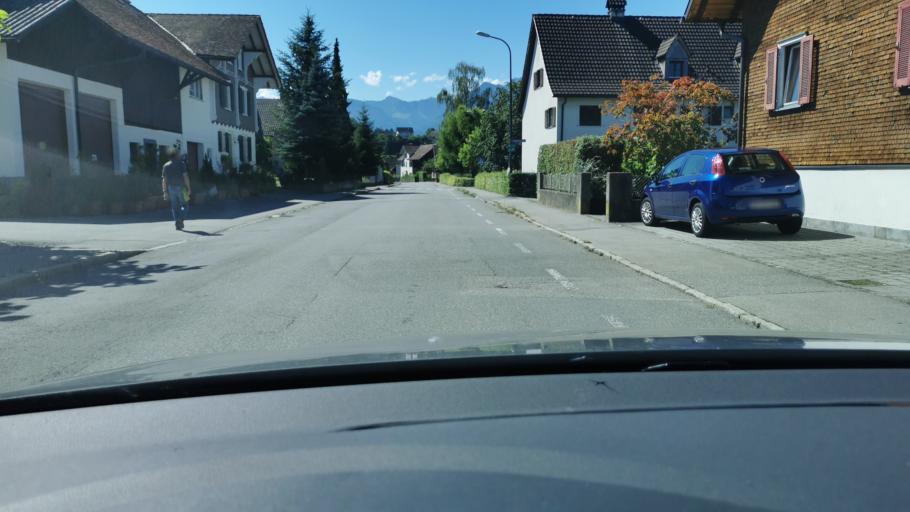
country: AT
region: Vorarlberg
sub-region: Politischer Bezirk Feldkirch
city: Rankweil
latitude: 47.2761
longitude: 9.6449
